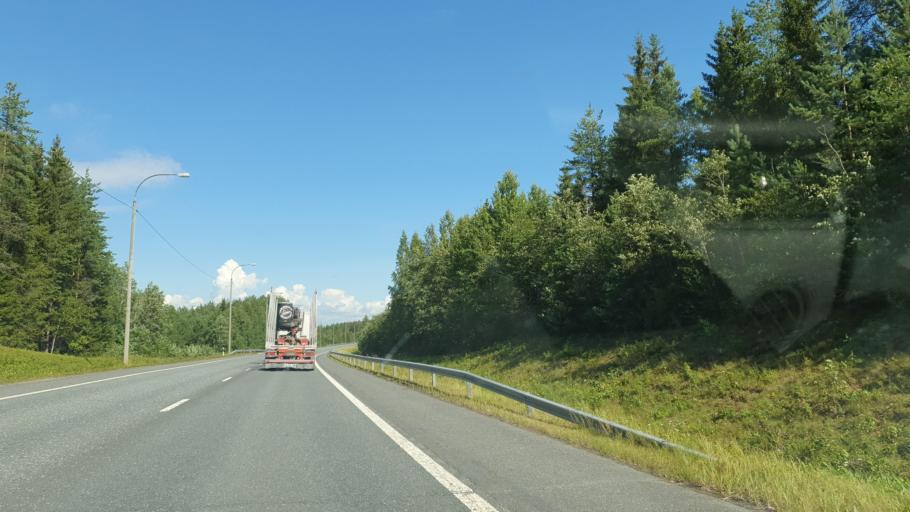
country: FI
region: Northern Savo
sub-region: Ylae-Savo
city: Iisalmi
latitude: 63.6044
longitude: 27.2155
